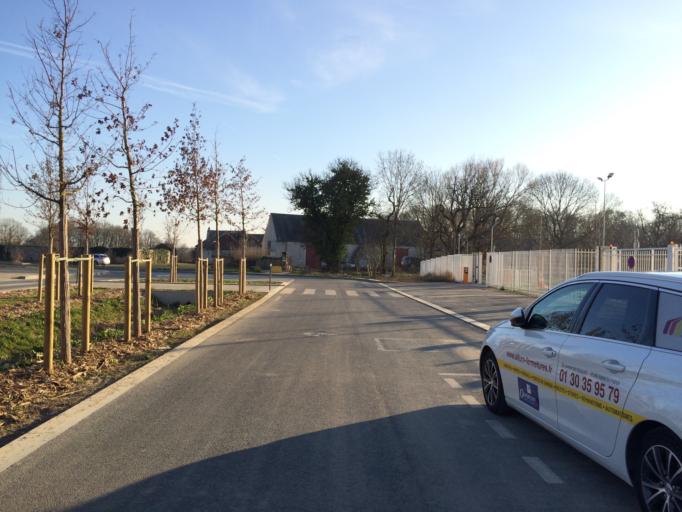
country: FR
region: Ile-de-France
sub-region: Departement de l'Essonne
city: Orsay
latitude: 48.7120
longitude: 2.2013
